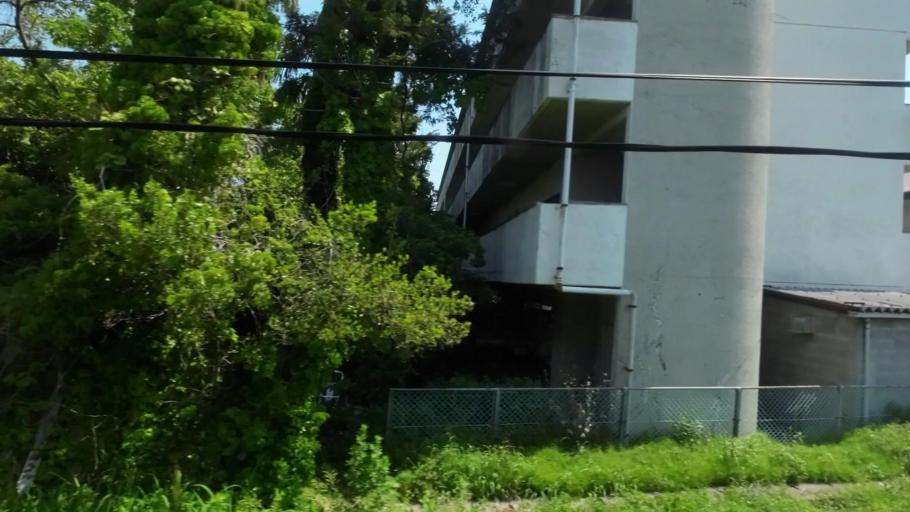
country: JP
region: Ehime
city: Saijo
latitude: 33.9334
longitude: 133.0823
